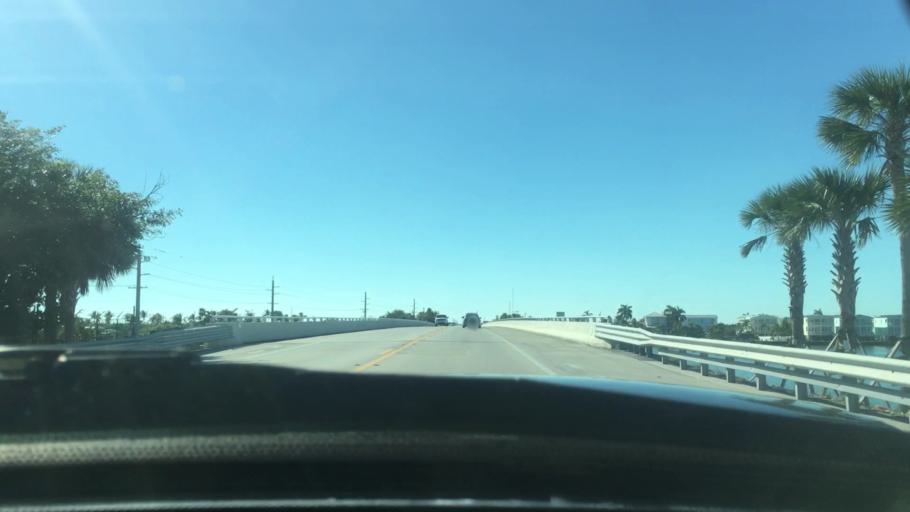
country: US
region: Florida
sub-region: Monroe County
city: Big Pine Key
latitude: 24.6672
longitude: -81.3834
